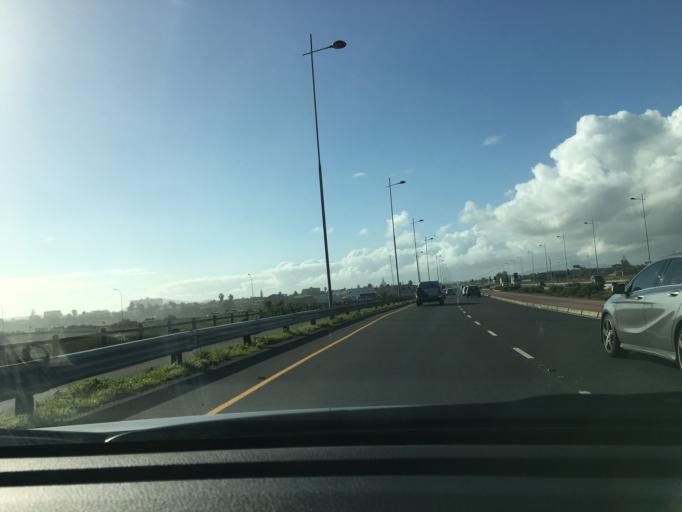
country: ZA
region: Western Cape
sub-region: City of Cape Town
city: Sunset Beach
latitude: -33.8318
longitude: 18.4843
